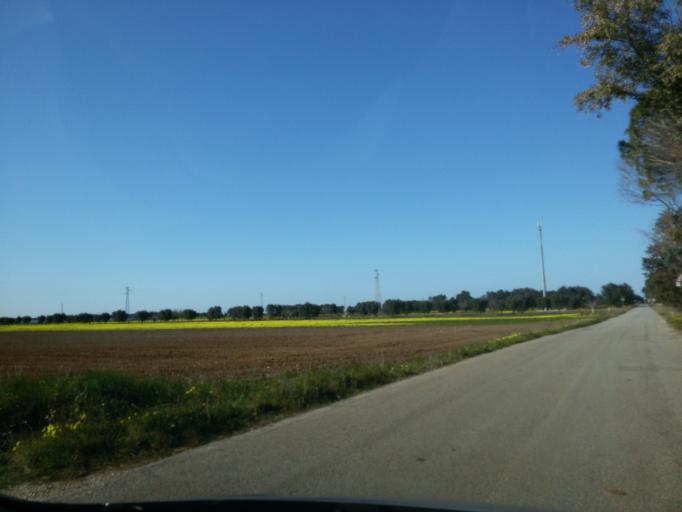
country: IT
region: Apulia
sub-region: Provincia di Brindisi
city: Mesagne
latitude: 40.6540
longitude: 17.8236
